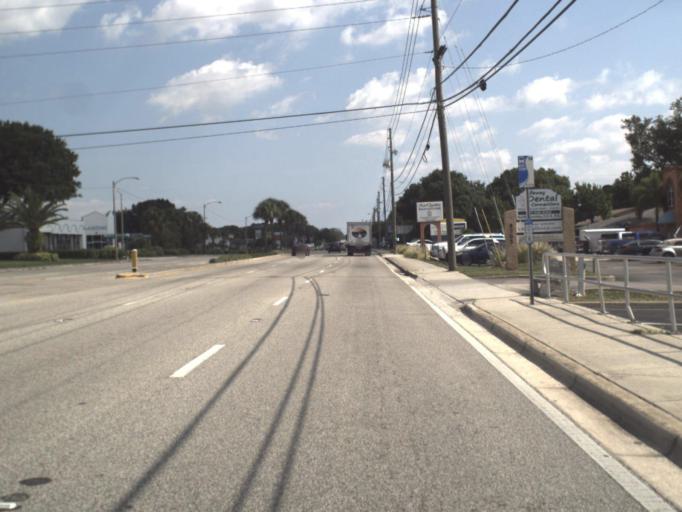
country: US
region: Florida
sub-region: Pinellas County
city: Seminole
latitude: 27.8566
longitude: -82.7870
